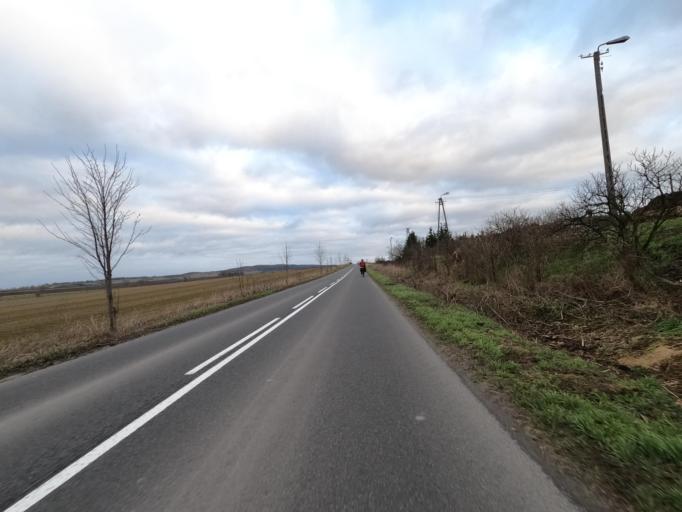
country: PL
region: Greater Poland Voivodeship
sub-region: Powiat pilski
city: Bialosliwie
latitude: 53.1102
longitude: 17.1546
